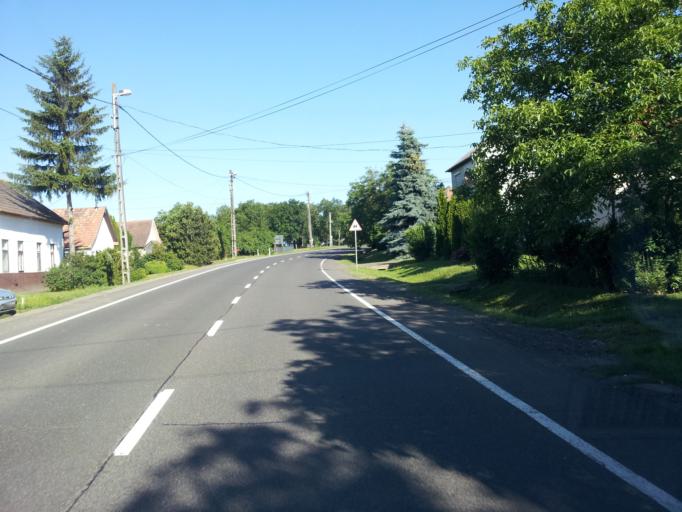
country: HU
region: Nograd
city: Nagyoroszi
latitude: 48.0082
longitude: 19.0809
